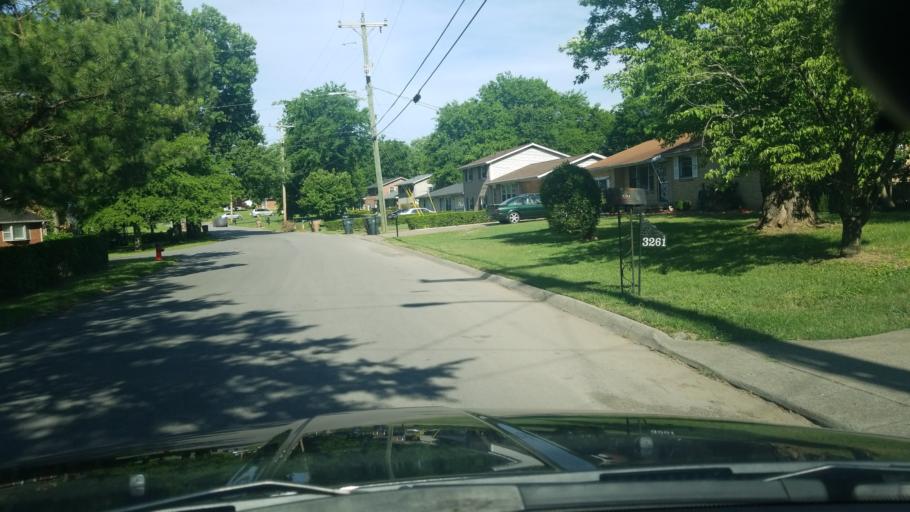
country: US
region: Tennessee
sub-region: Davidson County
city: Nashville
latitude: 36.2391
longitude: -86.7739
